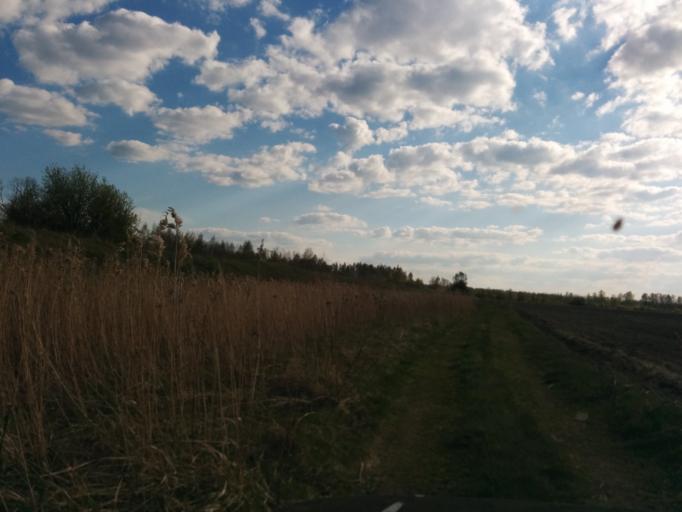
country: LV
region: Jelgava
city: Jelgava
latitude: 56.6797
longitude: 23.6924
